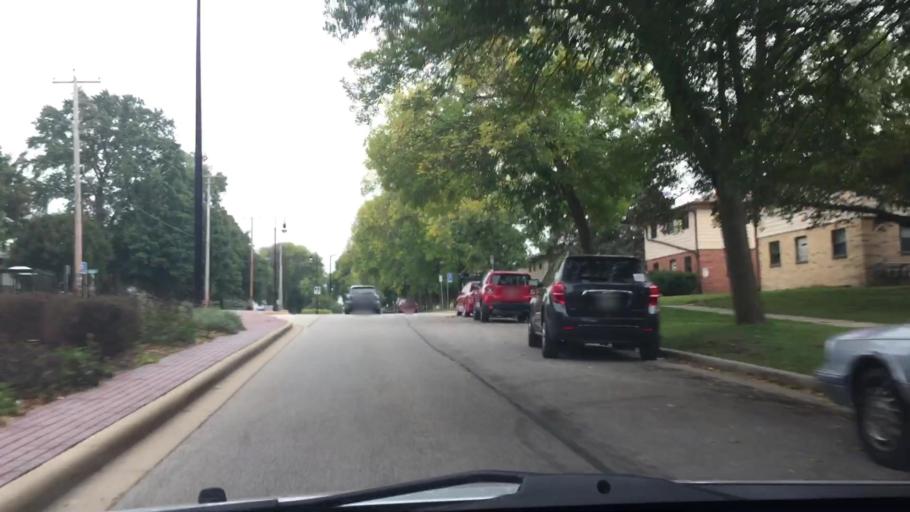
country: US
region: Wisconsin
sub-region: Waukesha County
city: Waukesha
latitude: 43.0014
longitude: -88.2320
